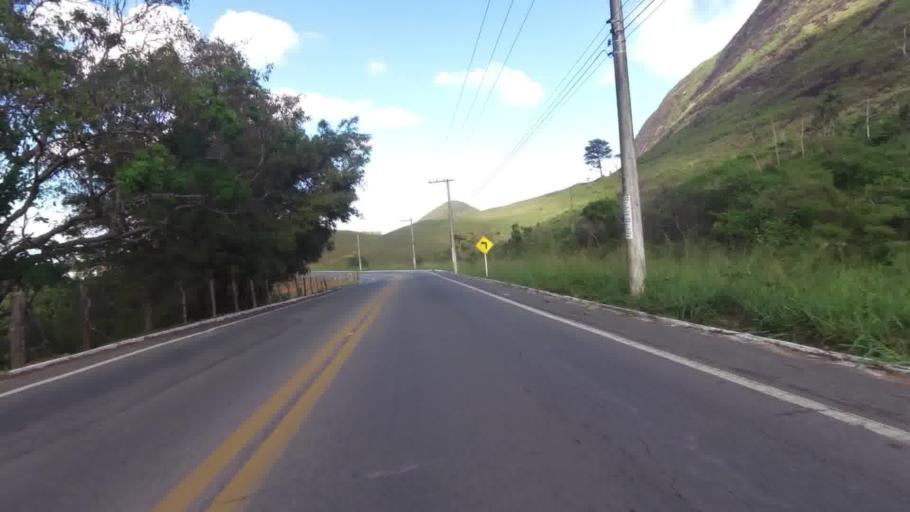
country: BR
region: Espirito Santo
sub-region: Piuma
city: Piuma
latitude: -20.8693
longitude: -40.7624
